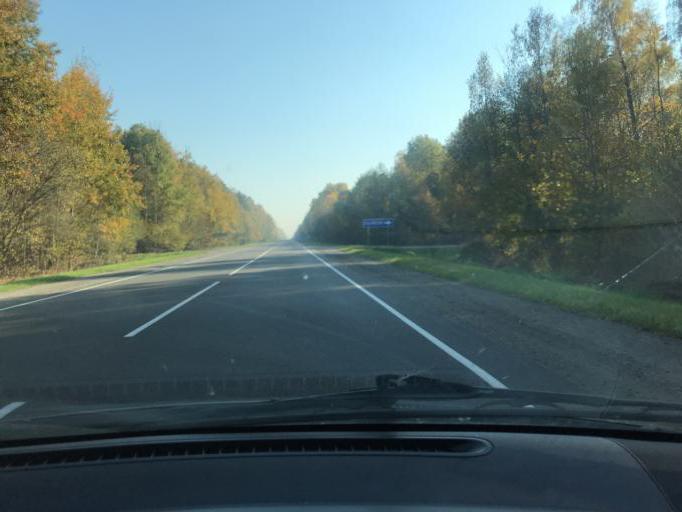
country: BY
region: Brest
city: Horad Luninyets
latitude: 52.3079
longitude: 26.6840
